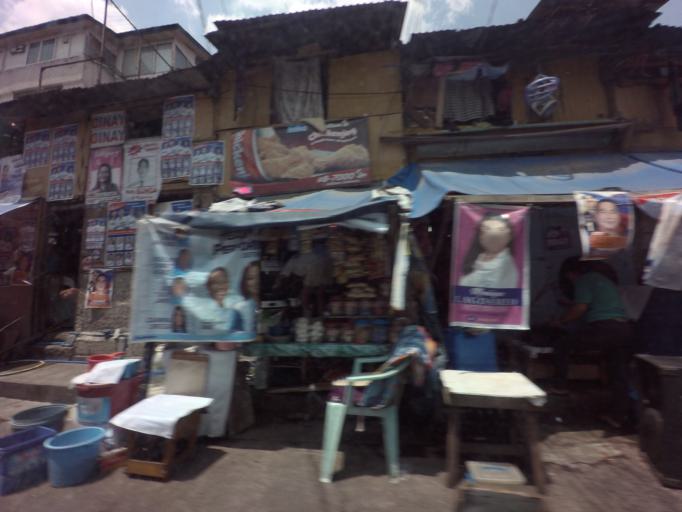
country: PH
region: Metro Manila
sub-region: Mandaluyong
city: Mandaluyong City
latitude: 14.5727
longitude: 121.0258
